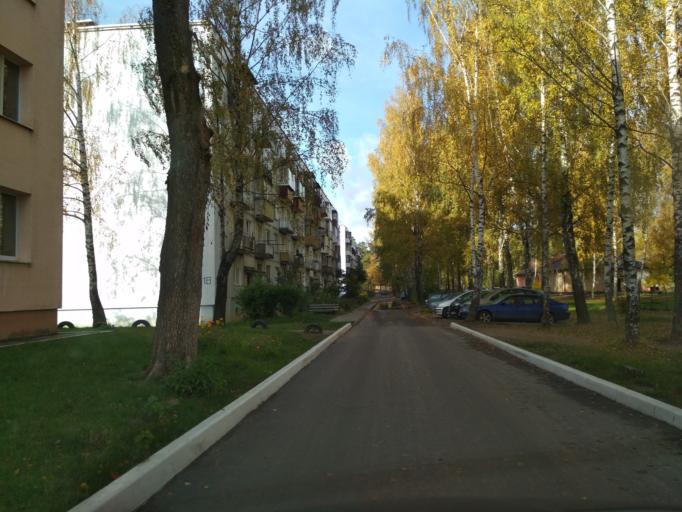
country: BY
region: Minsk
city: Mar''ina Horka
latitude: 53.5027
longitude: 28.1702
